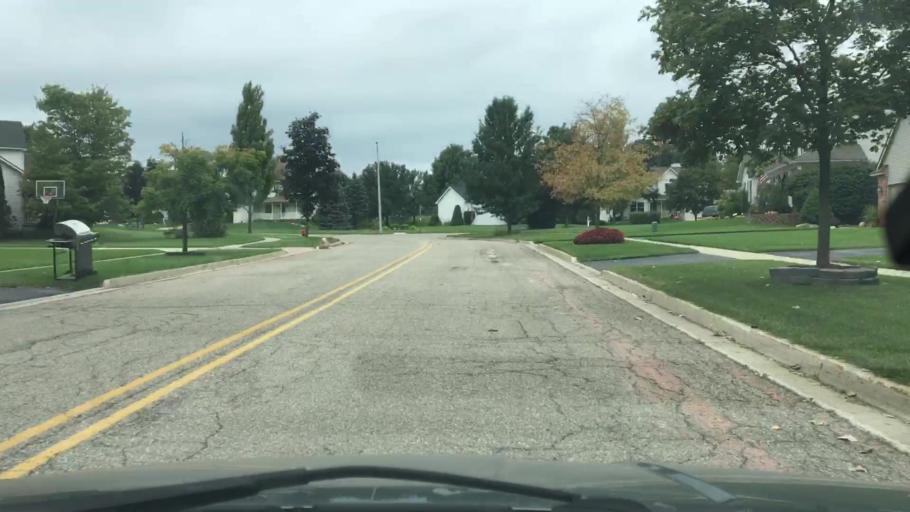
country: US
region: Michigan
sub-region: Livingston County
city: Brighton
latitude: 42.5146
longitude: -83.7827
